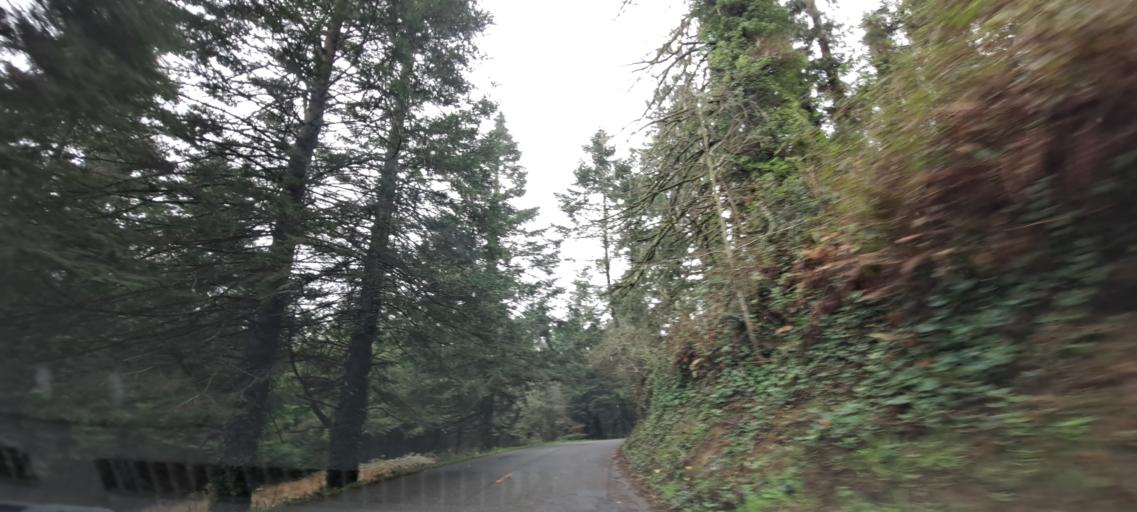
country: US
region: California
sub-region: Humboldt County
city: Fortuna
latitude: 40.5972
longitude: -124.1428
